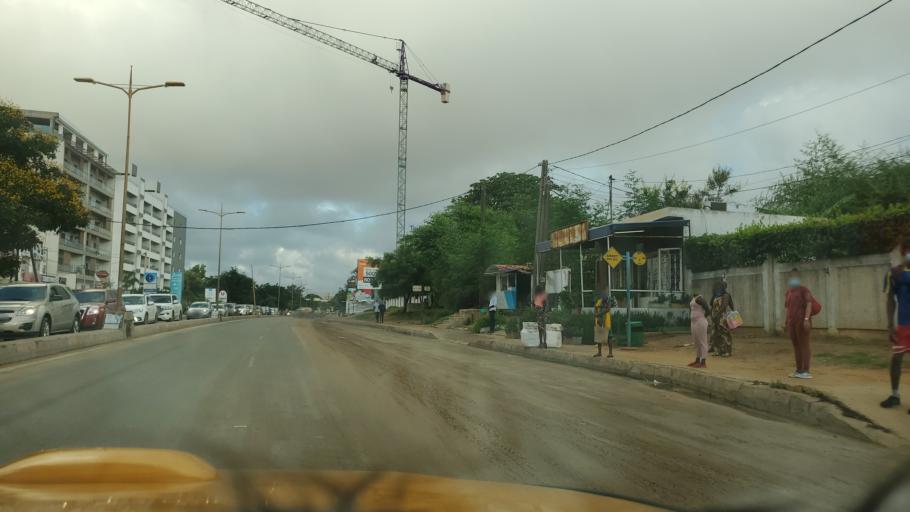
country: SN
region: Dakar
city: Mermoz Boabab
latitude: 14.7177
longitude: -17.4864
